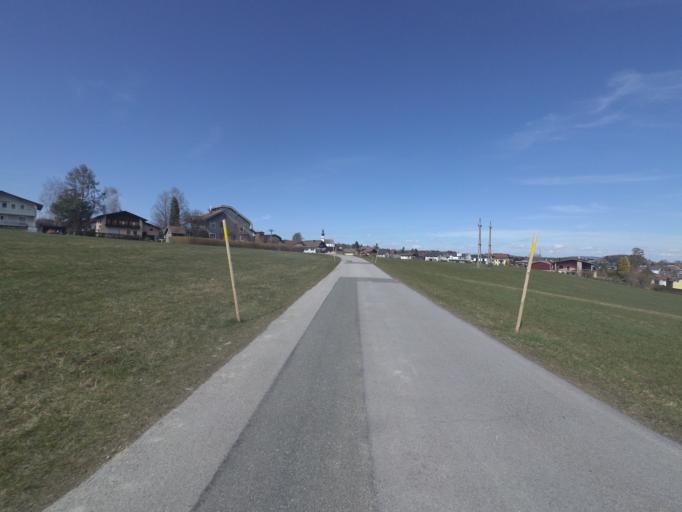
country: AT
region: Salzburg
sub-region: Politischer Bezirk Salzburg-Umgebung
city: Seekirchen am Wallersee
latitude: 47.8944
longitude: 13.1140
